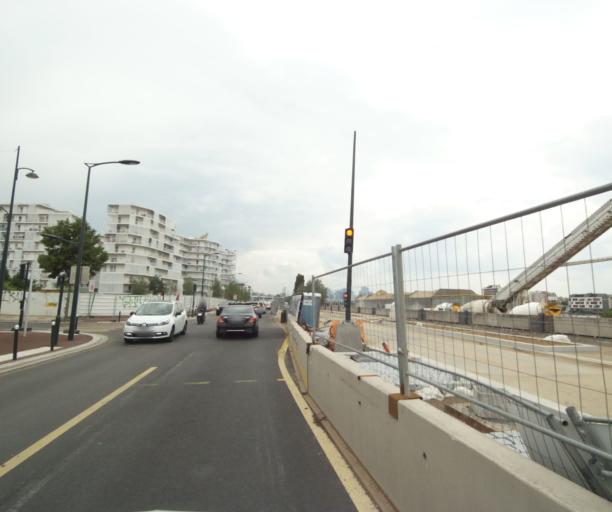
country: FR
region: Ile-de-France
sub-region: Departement des Hauts-de-Seine
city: Levallois-Perret
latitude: 48.9052
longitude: 2.2935
